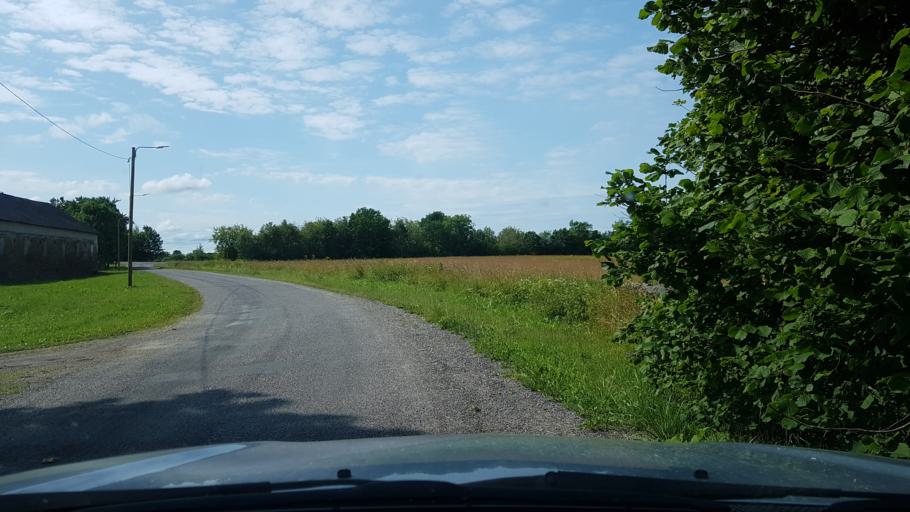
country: EE
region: Ida-Virumaa
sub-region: Sillamaee linn
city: Sillamae
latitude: 59.3761
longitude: 27.8789
